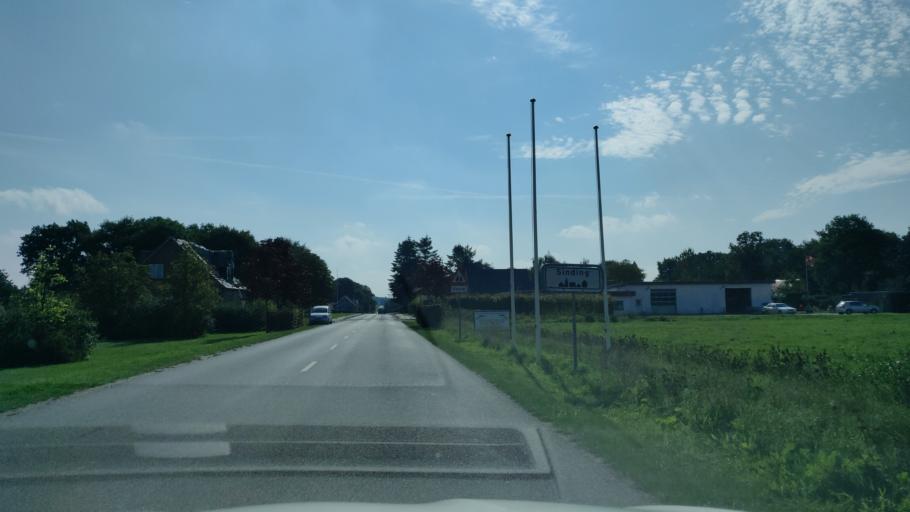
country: DK
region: Central Jutland
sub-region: Herning Kommune
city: Avlum
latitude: 56.2155
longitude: 8.8494
